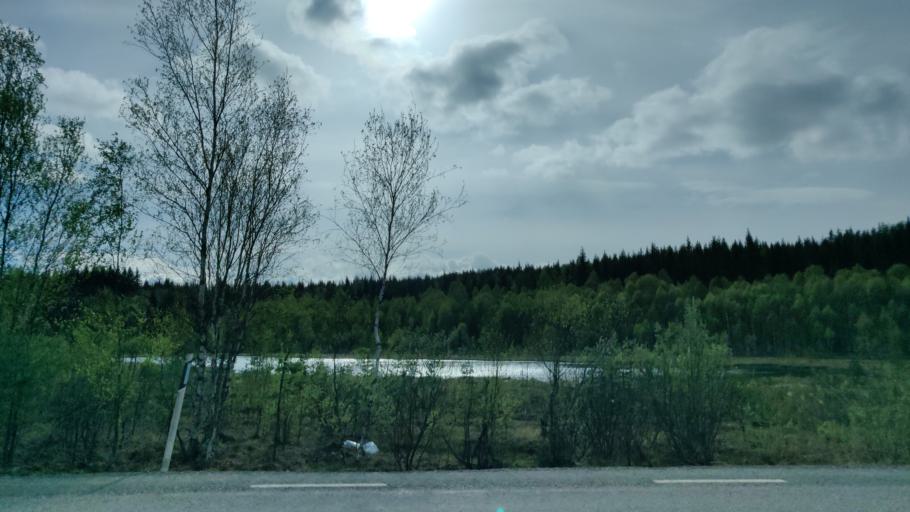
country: SE
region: Vaermland
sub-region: Forshaga Kommun
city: Deje
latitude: 59.5993
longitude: 13.4505
